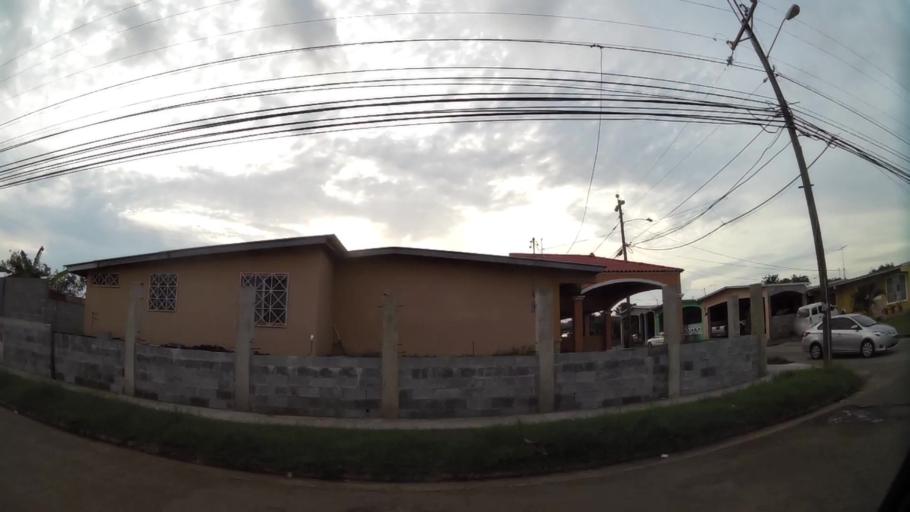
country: PA
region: Panama
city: Tocumen
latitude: 9.0941
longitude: -79.3873
